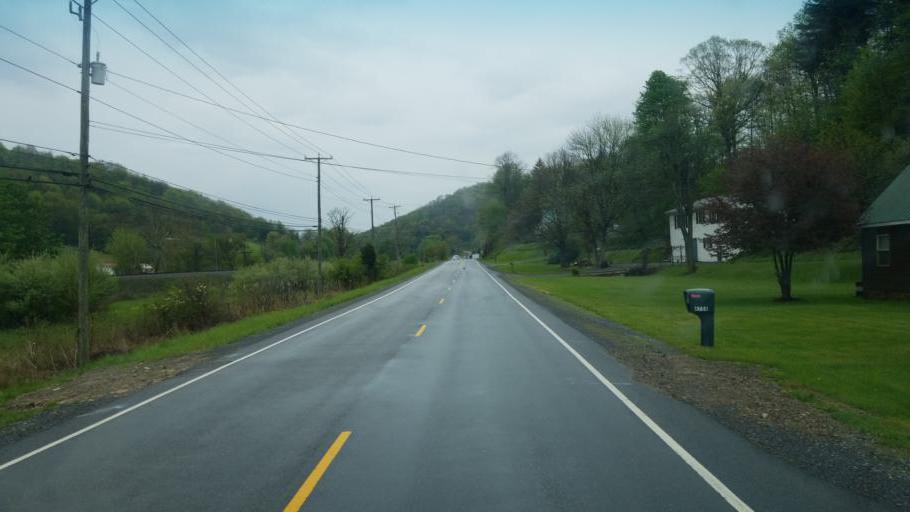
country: US
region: Virginia
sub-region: Smyth County
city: Atkins
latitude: 36.8763
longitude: -81.3893
